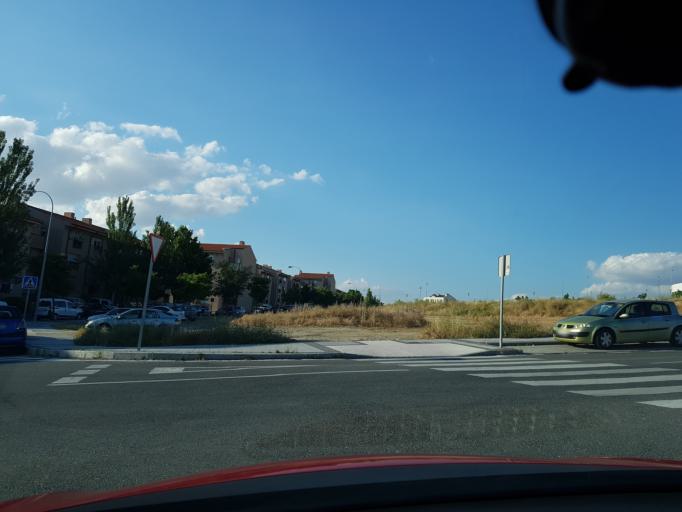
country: ES
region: Castille and Leon
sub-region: Provincia de Segovia
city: Segovia
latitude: 40.9345
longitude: -4.1063
